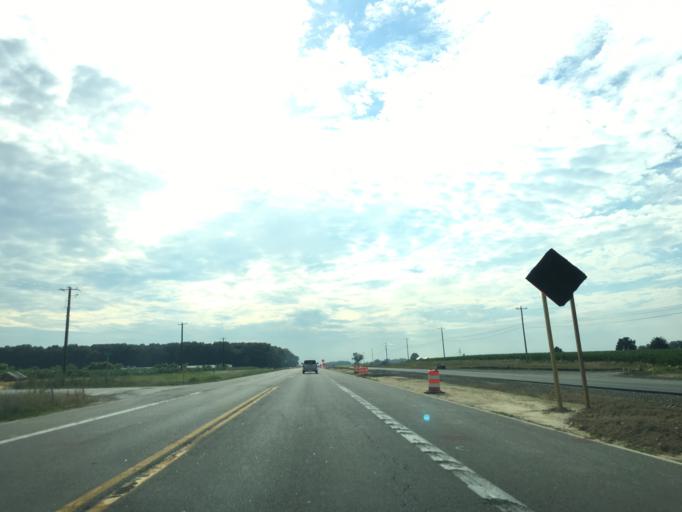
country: US
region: Maryland
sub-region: Caroline County
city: Ridgely
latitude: 38.9270
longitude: -75.9952
